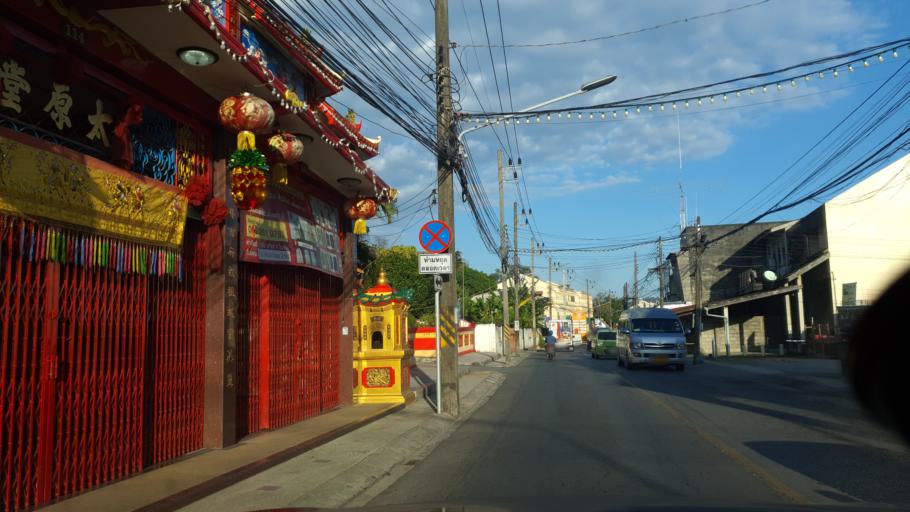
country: TH
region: Phuket
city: Ban Talat Nua
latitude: 7.8850
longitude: 98.3827
